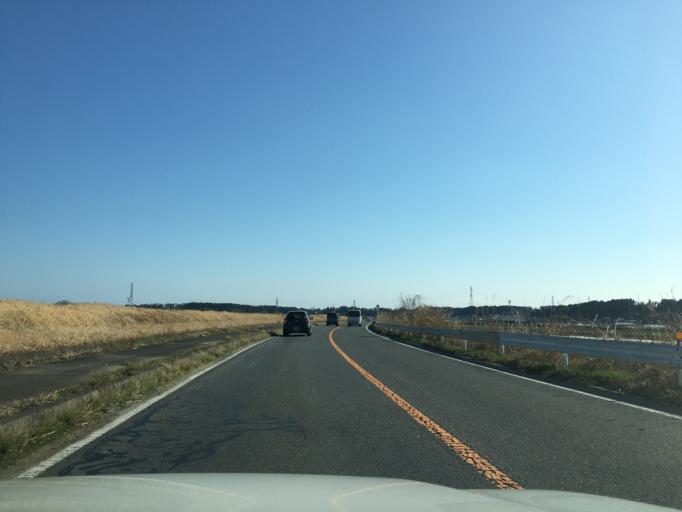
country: JP
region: Ibaraki
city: Mito-shi
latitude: 36.4318
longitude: 140.4205
